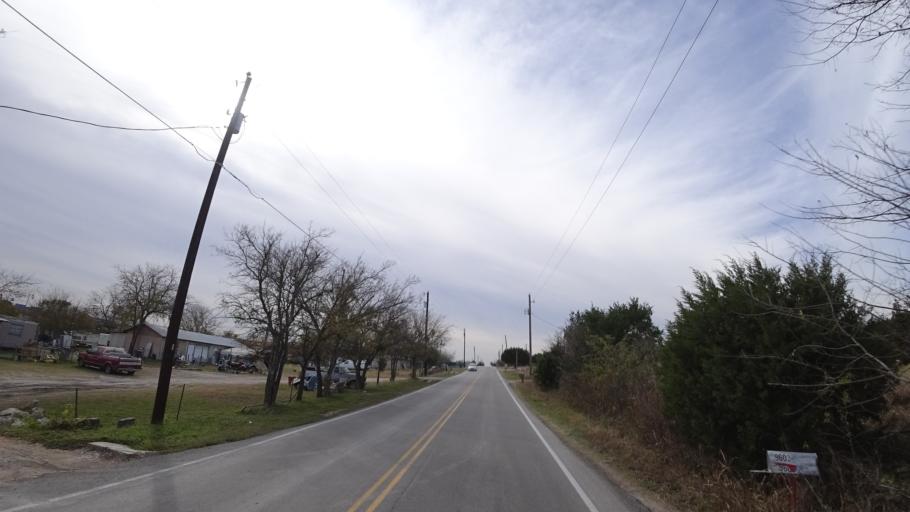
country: US
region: Texas
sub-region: Travis County
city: Onion Creek
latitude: 30.1355
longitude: -97.7337
